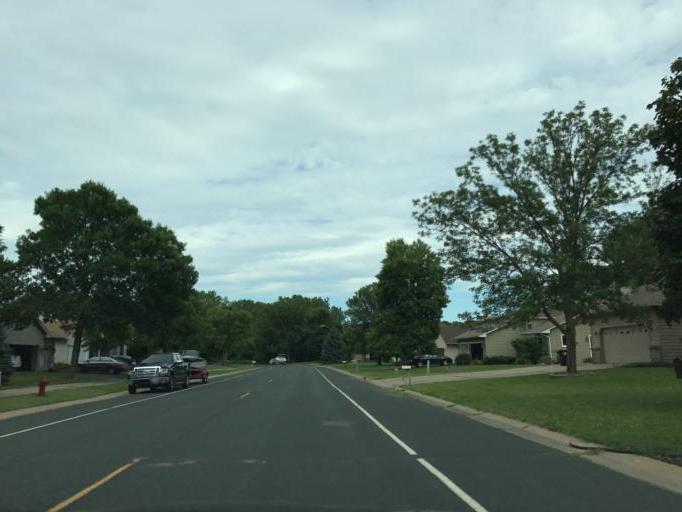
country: US
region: Minnesota
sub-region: Hennepin County
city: Maple Grove
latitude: 45.0837
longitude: -93.4199
